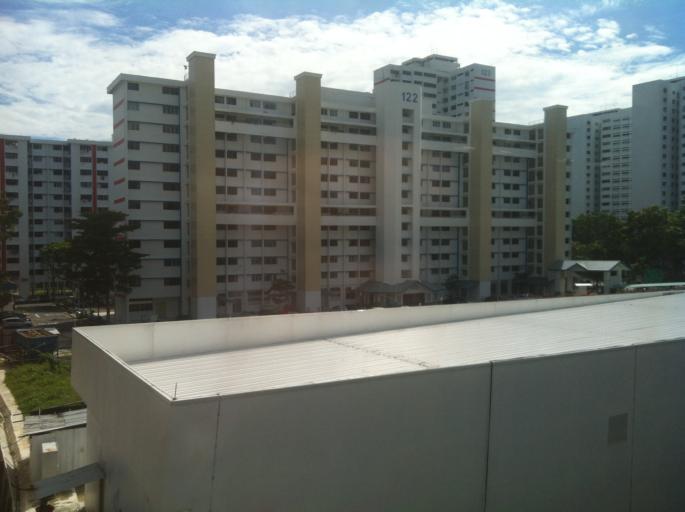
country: SG
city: Singapore
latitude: 1.3169
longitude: 103.8845
